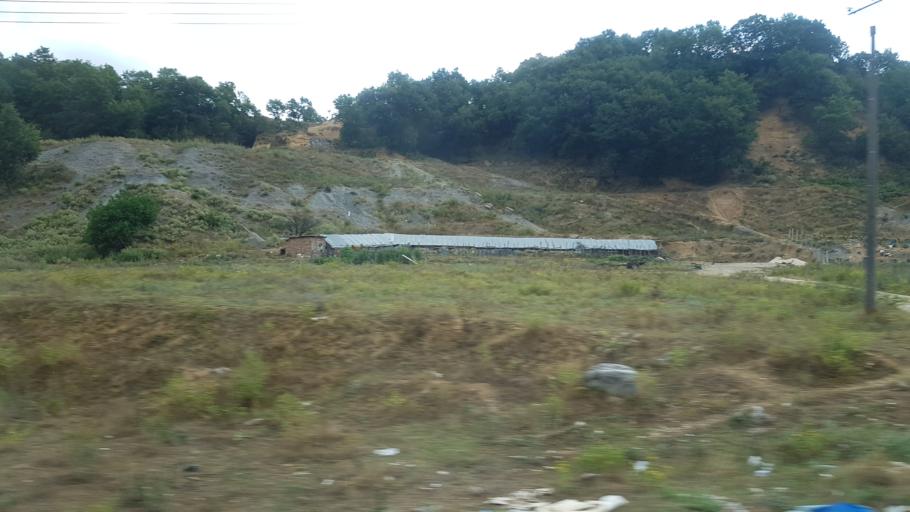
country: AL
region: Vlore
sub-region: Rrethi i Sarandes
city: Dhiver
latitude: 39.9134
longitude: 20.1844
